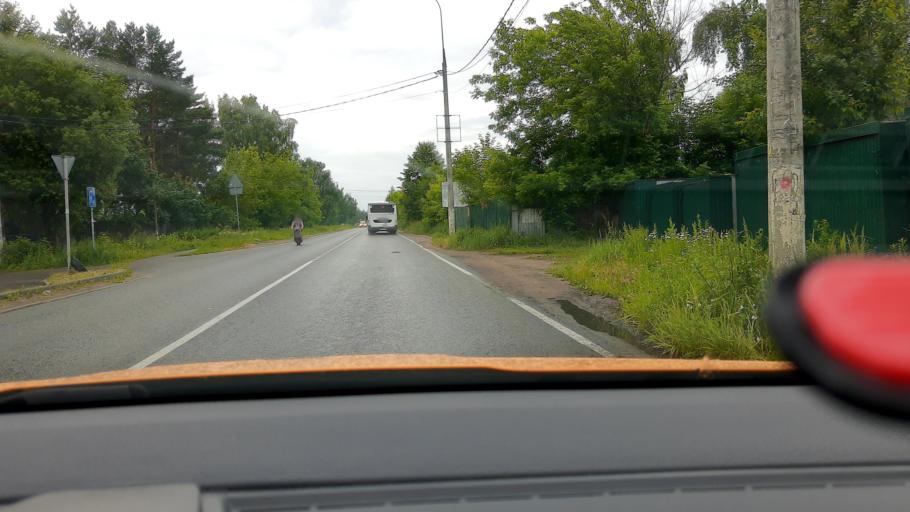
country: RU
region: Moskovskaya
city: Pirogovskiy
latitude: 55.9955
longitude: 37.6709
